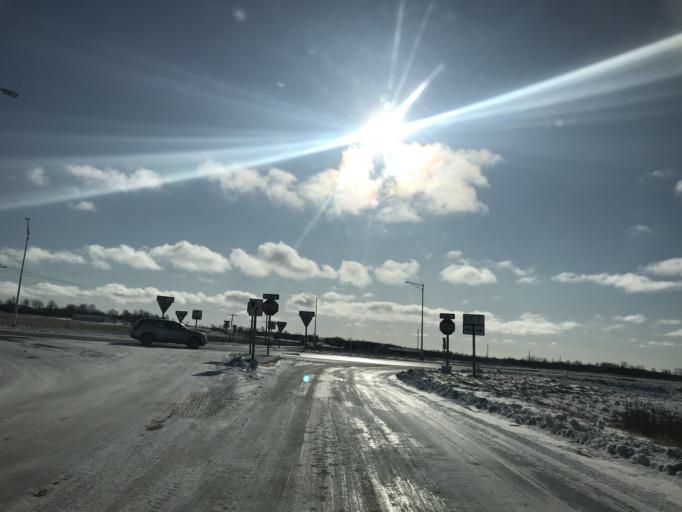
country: US
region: Wisconsin
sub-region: Kewaunee County
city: Luxemburg
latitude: 44.7178
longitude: -87.6210
